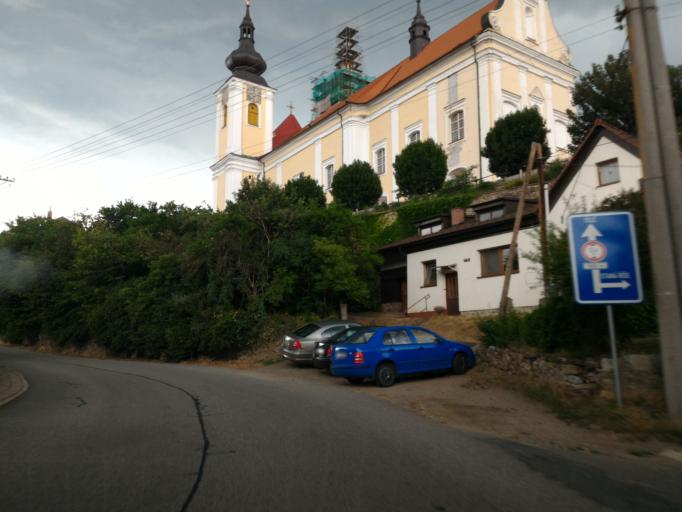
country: CZ
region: Vysocina
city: Zeletava
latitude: 49.1384
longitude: 15.5655
